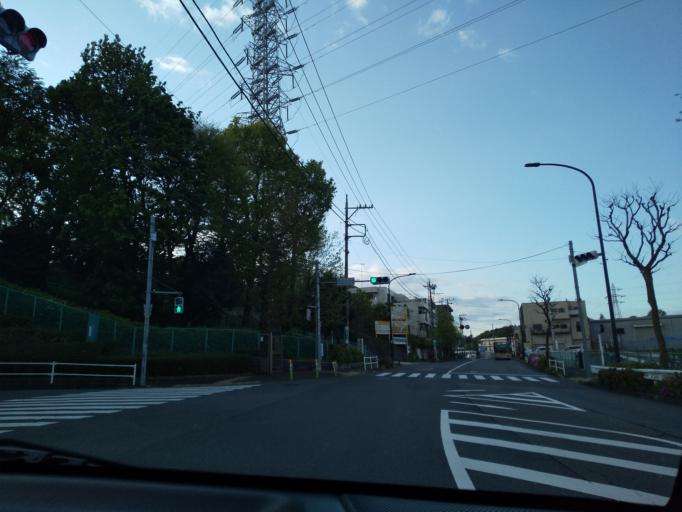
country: JP
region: Tokyo
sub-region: Machida-shi
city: Machida
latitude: 35.5551
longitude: 139.4276
